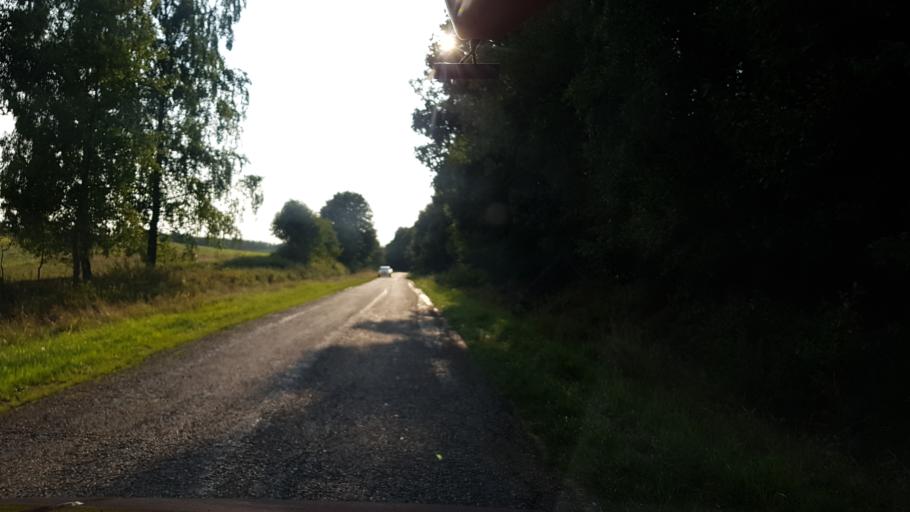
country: PL
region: West Pomeranian Voivodeship
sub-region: Powiat szczecinecki
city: Bialy Bor
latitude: 53.9812
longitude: 16.8839
